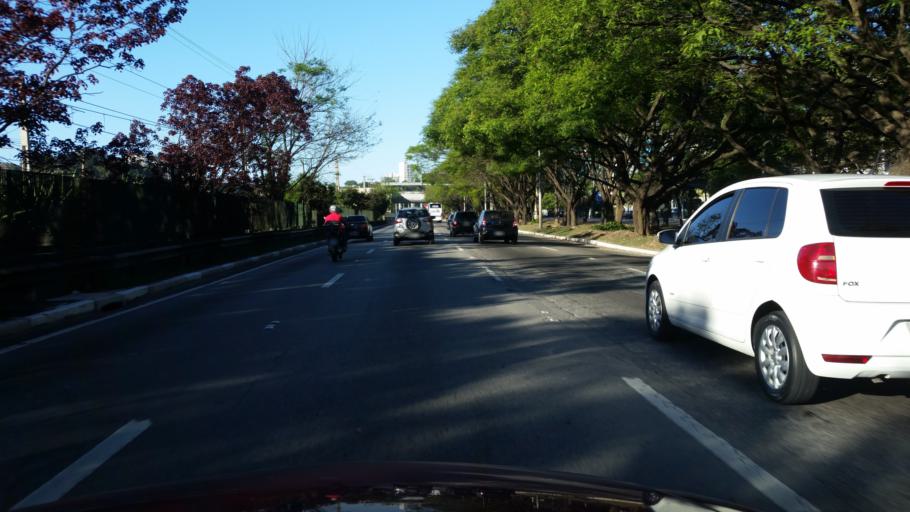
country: BR
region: Sao Paulo
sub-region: Taboao Da Serra
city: Taboao da Serra
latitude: -23.6295
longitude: -46.7135
